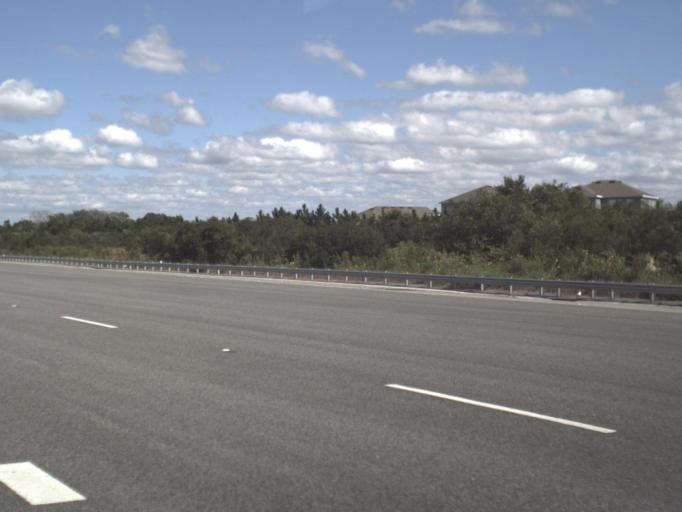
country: US
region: Florida
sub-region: Osceola County
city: Saint Cloud
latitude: 28.1780
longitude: -81.3027
